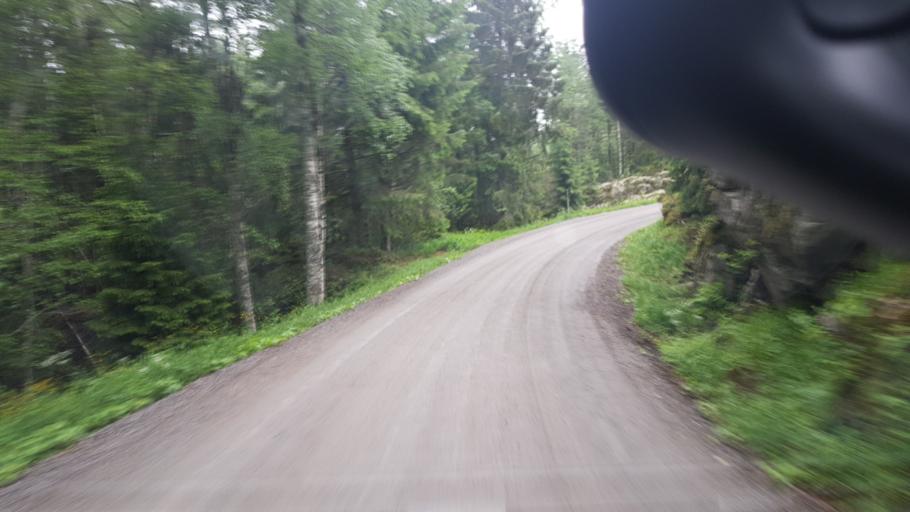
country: NO
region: Ostfold
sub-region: Romskog
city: Romskog
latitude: 59.7164
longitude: 11.9876
